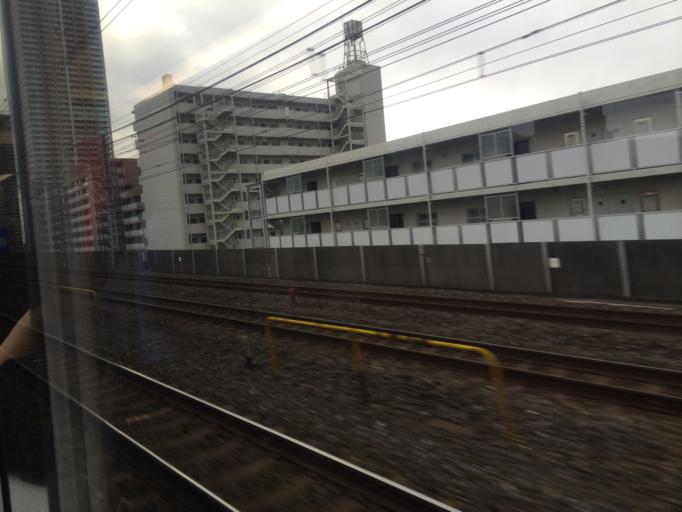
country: JP
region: Chiba
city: Matsudo
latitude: 35.7313
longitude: 139.9026
